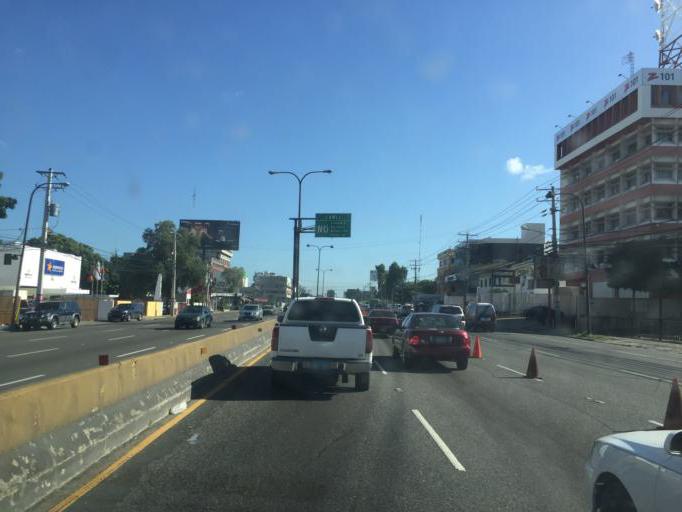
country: DO
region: Nacional
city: Bella Vista
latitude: 18.4606
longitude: -69.9401
